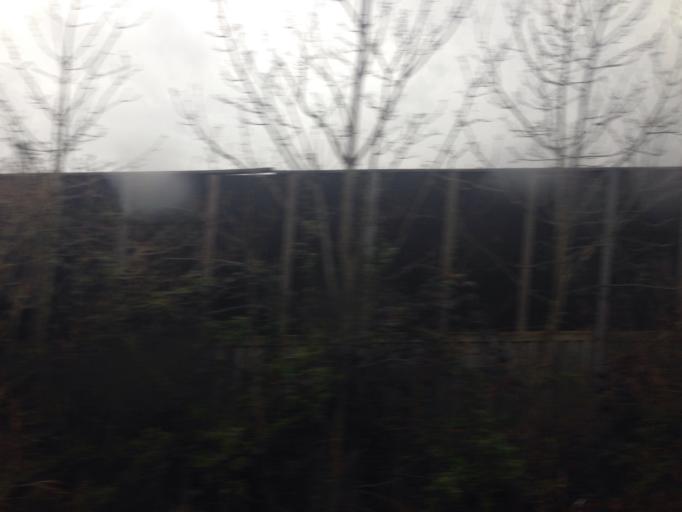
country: GB
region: England
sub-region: Greater London
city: Carshalton
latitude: 51.3765
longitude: -0.1543
